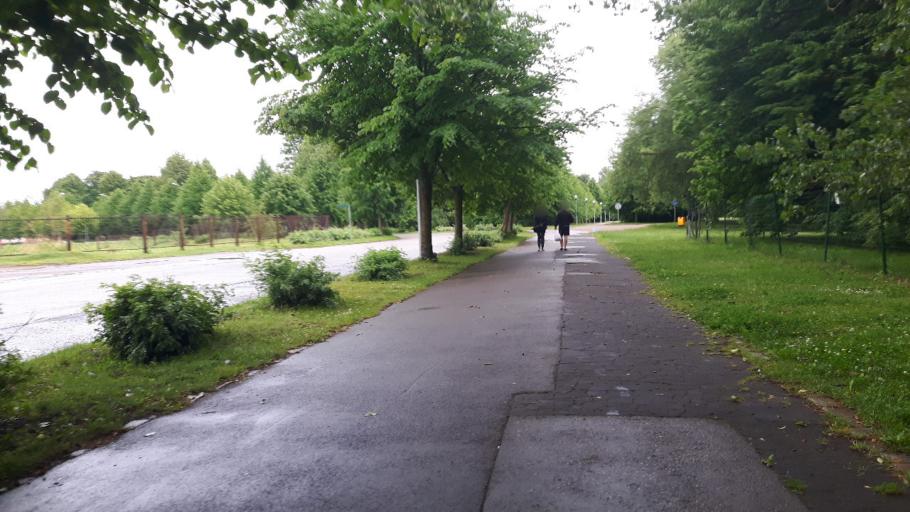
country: LV
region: Liepaja
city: Liepaja
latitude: 56.5112
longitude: 20.9924
